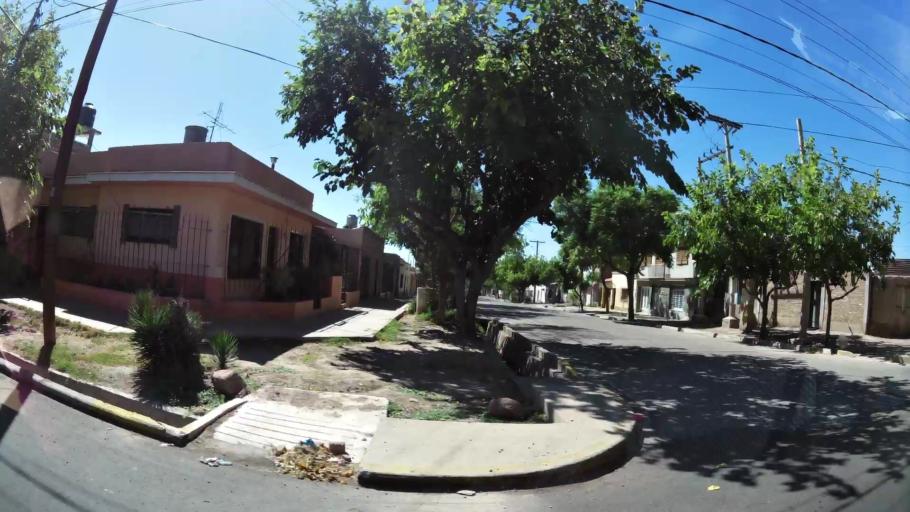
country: AR
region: Mendoza
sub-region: Departamento de Godoy Cruz
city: Godoy Cruz
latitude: -32.9174
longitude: -68.8638
